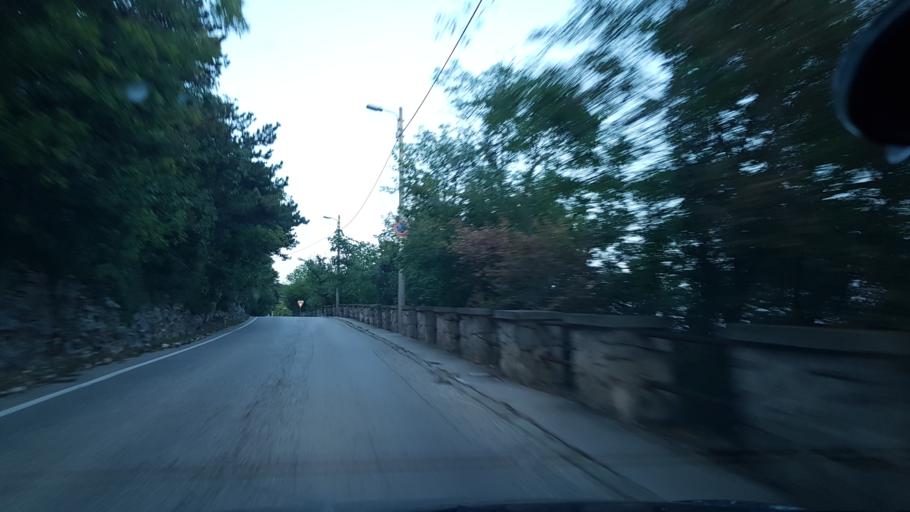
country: IT
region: Friuli Venezia Giulia
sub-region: Provincia di Trieste
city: Villa Opicina
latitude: 45.6794
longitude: 13.7779
